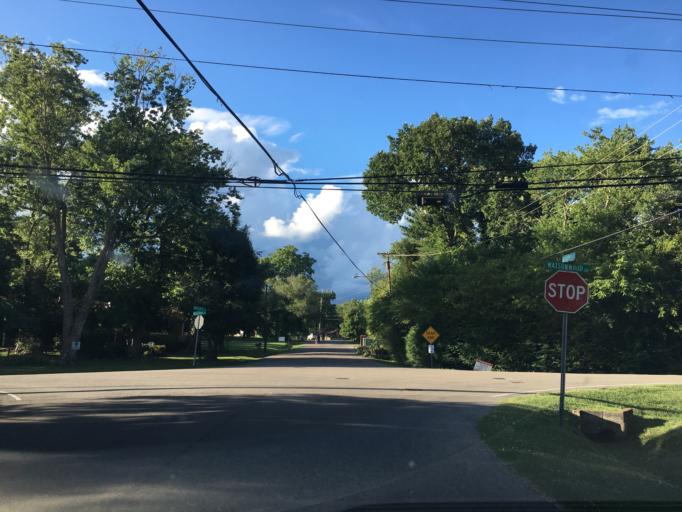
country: US
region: Tennessee
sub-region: Davidson County
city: Oak Hill
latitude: 36.0651
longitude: -86.7351
